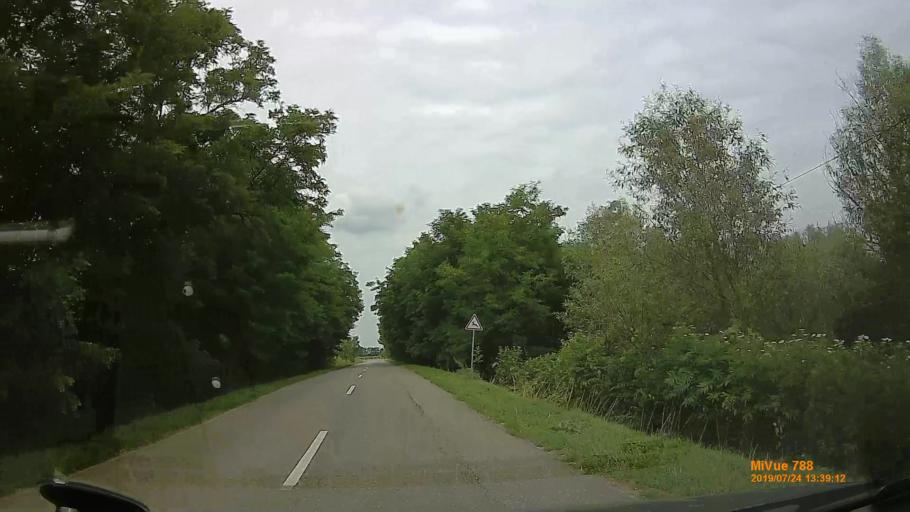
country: HU
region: Szabolcs-Szatmar-Bereg
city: Aranyosapati
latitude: 48.2372
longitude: 22.3196
